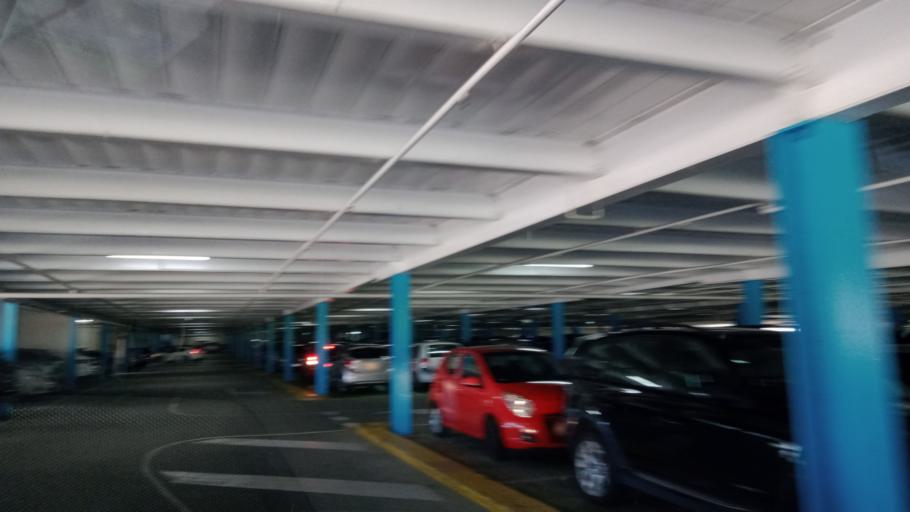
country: AU
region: Victoria
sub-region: Greater Dandenong
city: Noble Park North
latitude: -37.9346
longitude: 145.1884
